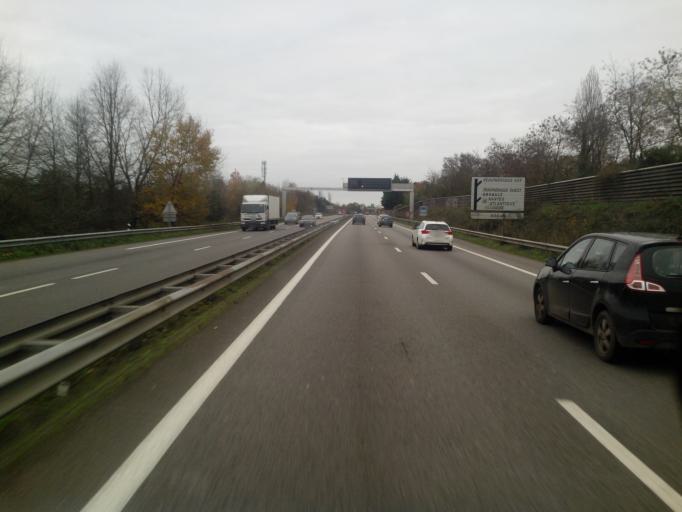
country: FR
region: Pays de la Loire
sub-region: Departement de la Loire-Atlantique
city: Orvault
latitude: 47.2739
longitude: -1.5938
